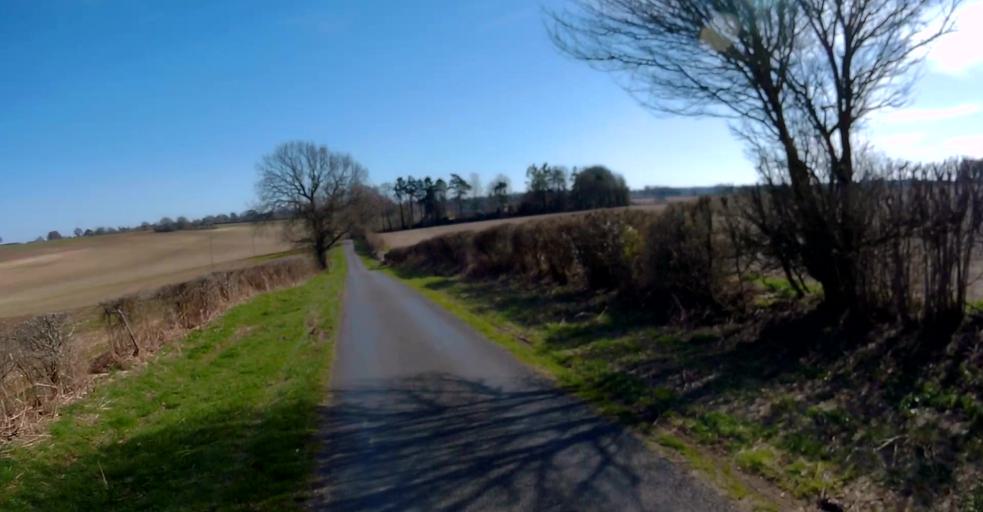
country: GB
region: England
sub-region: Hampshire
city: Four Marks
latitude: 51.1677
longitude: -1.0624
